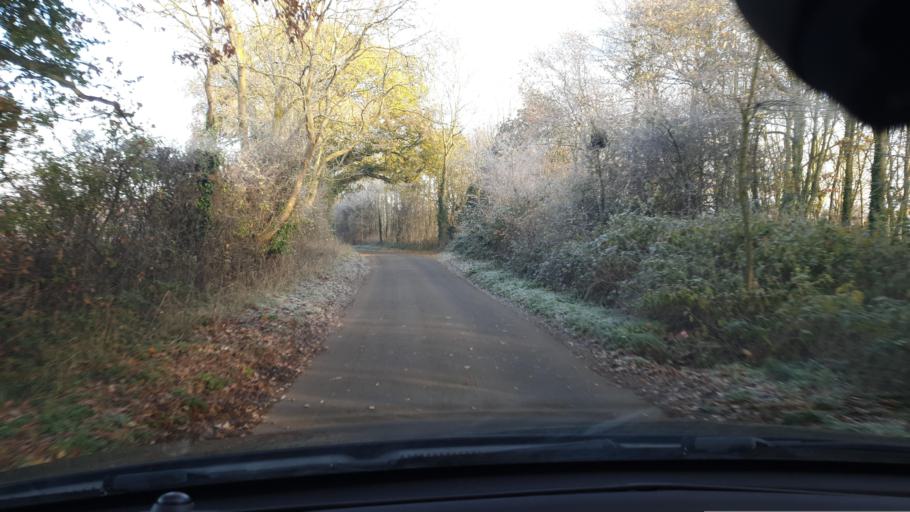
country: GB
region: England
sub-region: Essex
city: Mistley
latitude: 51.9816
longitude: 1.1136
